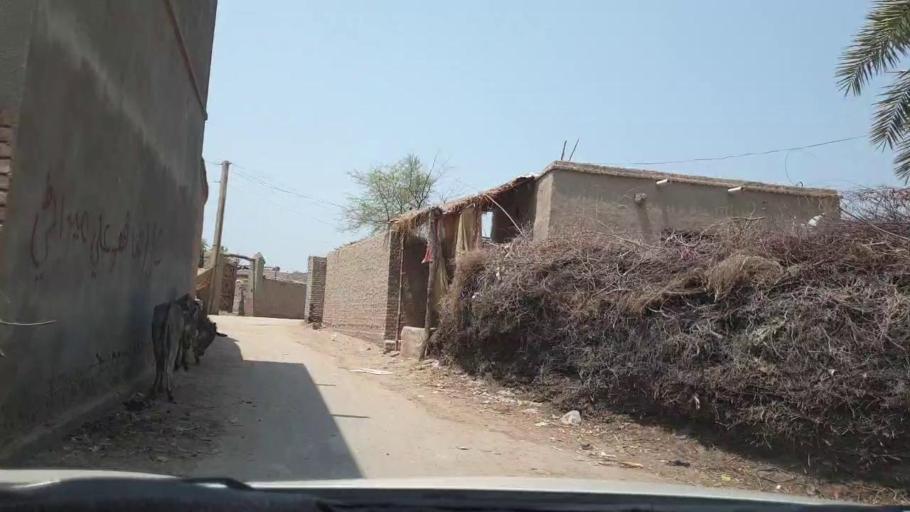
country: PK
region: Sindh
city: Radhan
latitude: 27.2402
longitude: 68.0062
